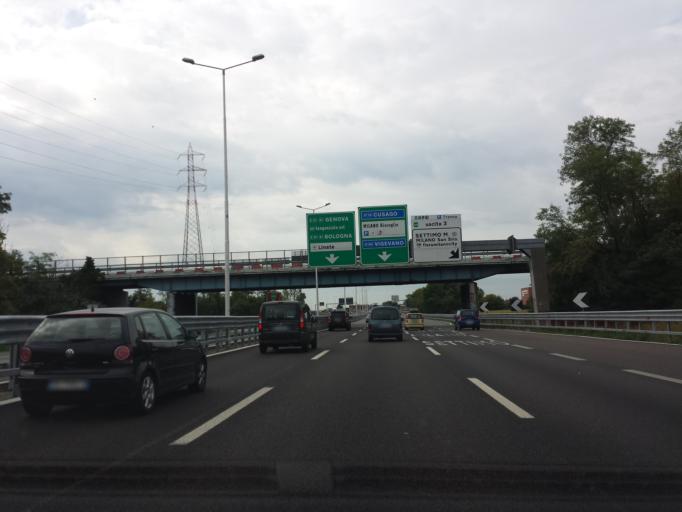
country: IT
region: Lombardy
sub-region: Citta metropolitana di Milano
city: Figino
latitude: 45.4939
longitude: 9.0665
